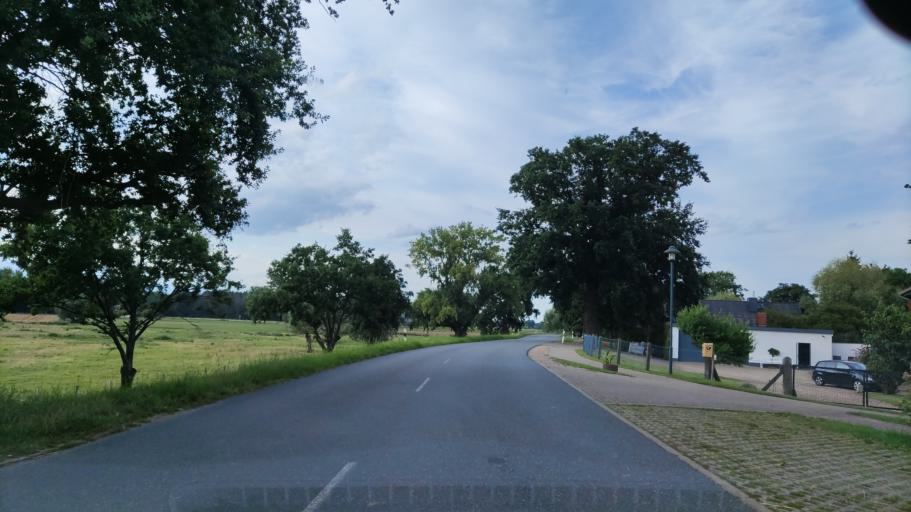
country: DE
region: Lower Saxony
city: Dannenberg
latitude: 53.1370
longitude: 11.1220
